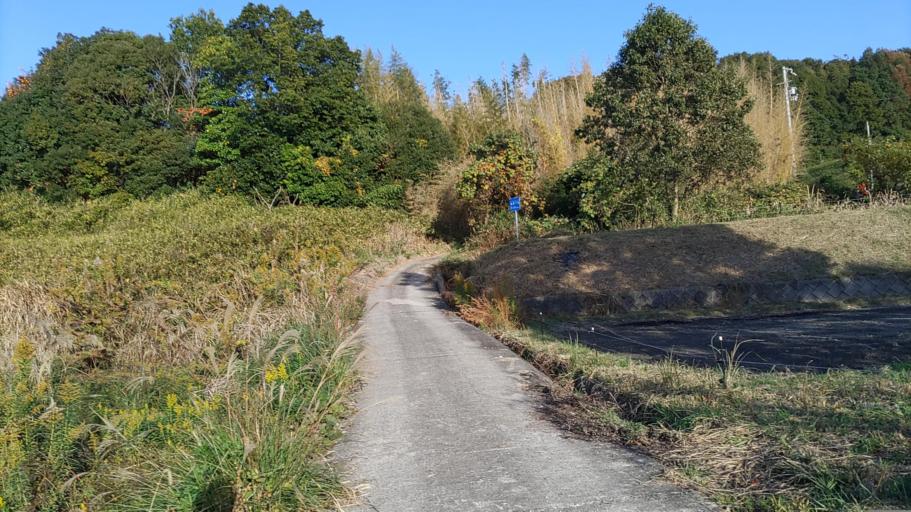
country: JP
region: Hyogo
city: Sumoto
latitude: 34.3844
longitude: 134.8173
